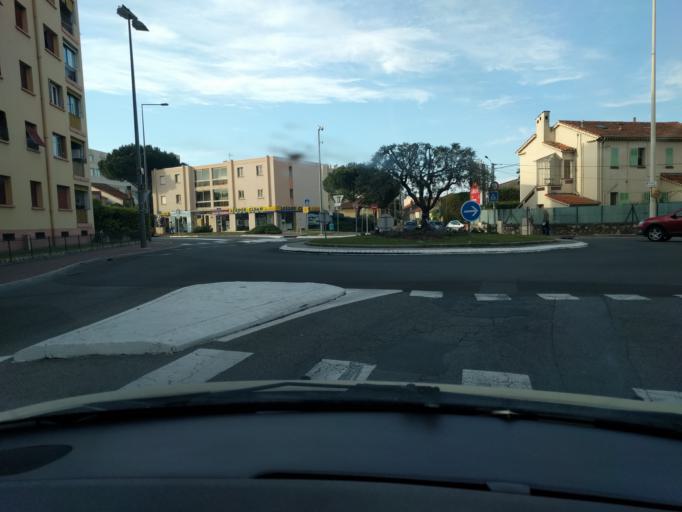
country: FR
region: Provence-Alpes-Cote d'Azur
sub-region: Departement des Alpes-Maritimes
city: Cannes
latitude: 43.5544
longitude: 6.9731
